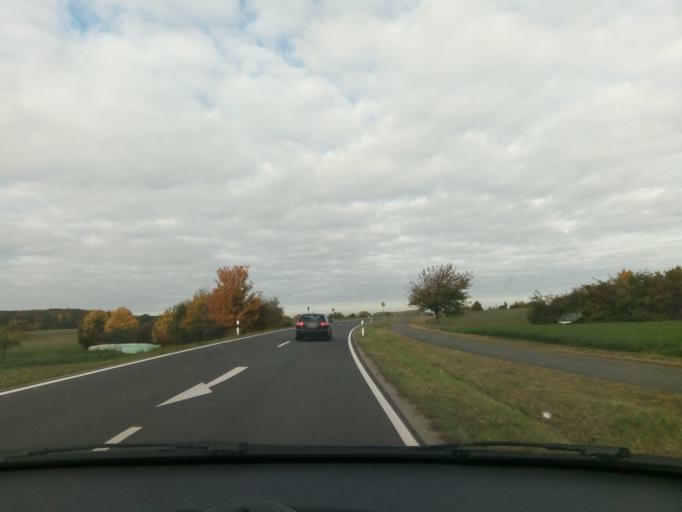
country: DE
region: Bavaria
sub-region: Regierungsbezirk Unterfranken
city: Dingolshausen
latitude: 49.8800
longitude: 10.3817
